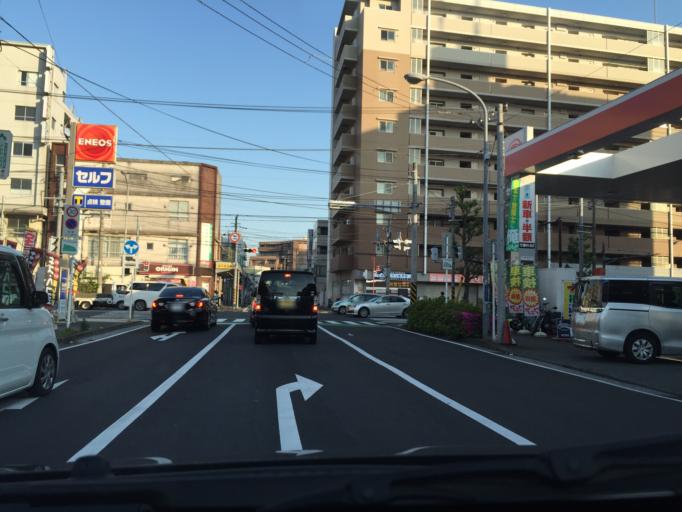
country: JP
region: Kanagawa
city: Yokohama
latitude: 35.4324
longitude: 139.6125
